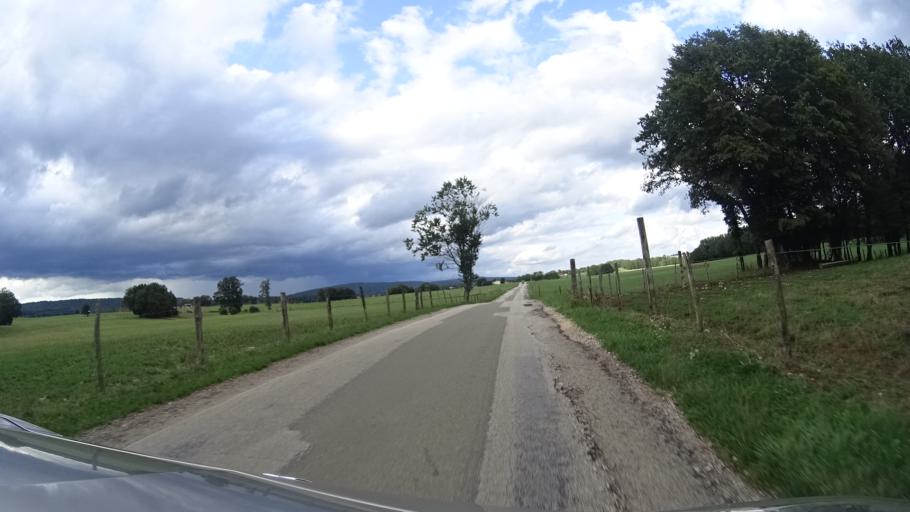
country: FR
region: Franche-Comte
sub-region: Departement du Doubs
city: Nancray
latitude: 47.2318
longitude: 6.1639
